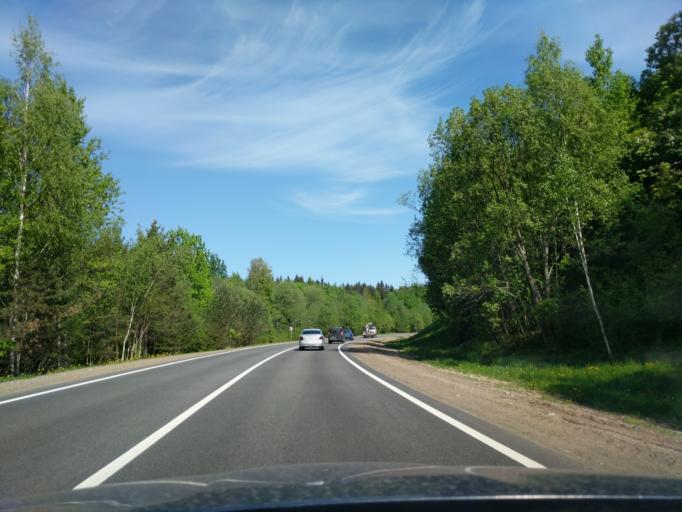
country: BY
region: Minsk
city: Bal'shavik
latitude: 54.1053
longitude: 27.5298
